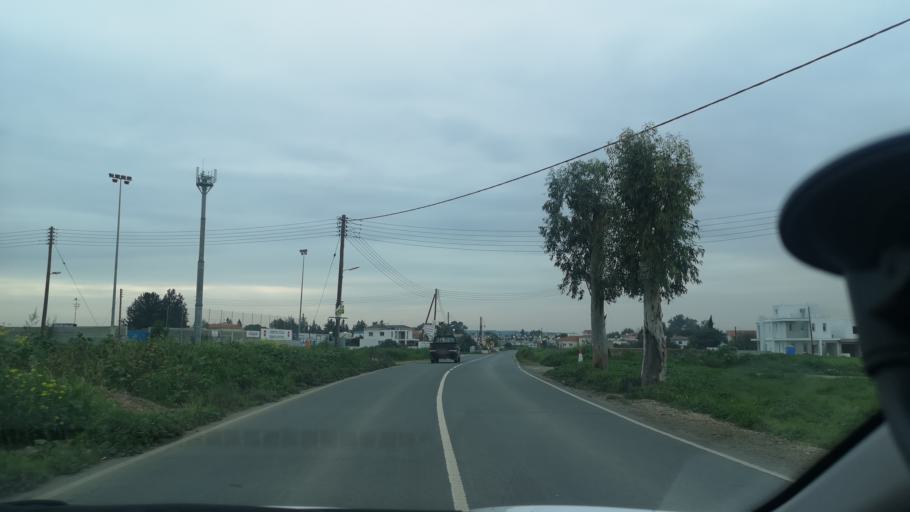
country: CY
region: Lefkosia
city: Kato Deftera
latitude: 35.0843
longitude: 33.2904
